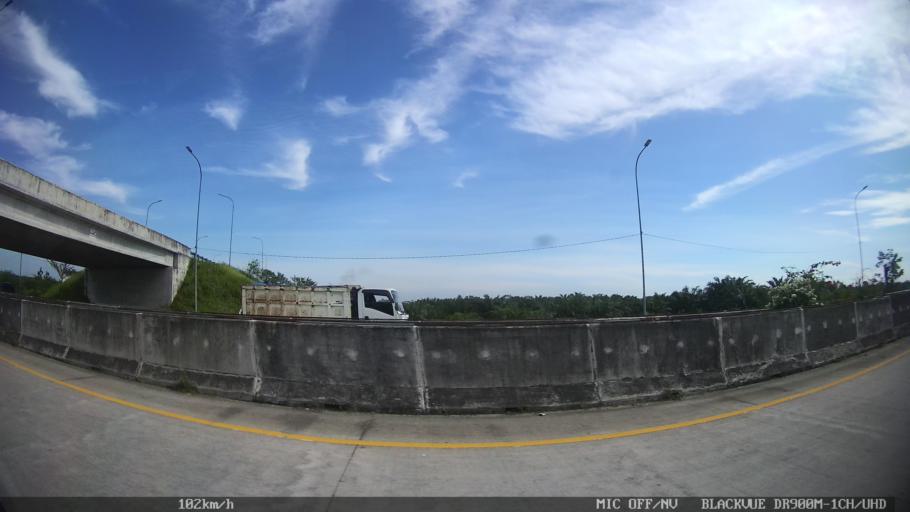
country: ID
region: North Sumatra
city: Sunggal
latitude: 3.6372
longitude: 98.5854
